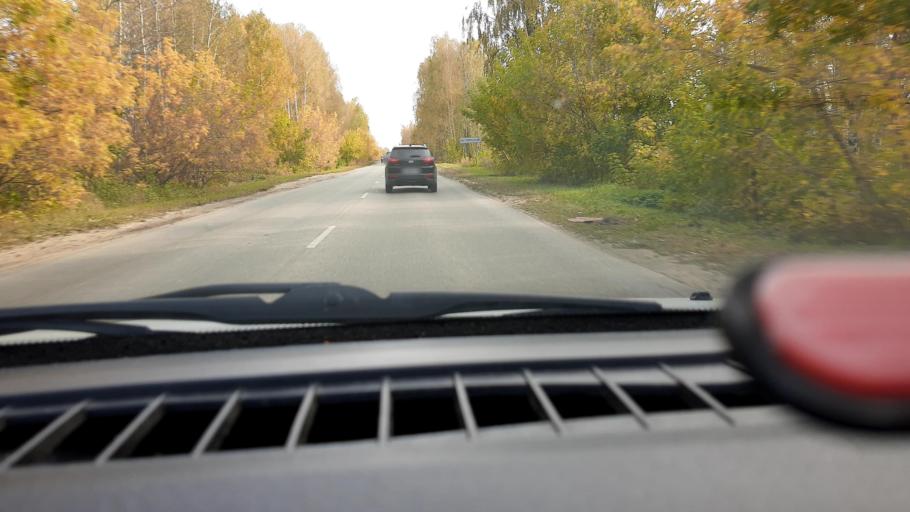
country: RU
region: Nizjnij Novgorod
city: Afonino
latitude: 56.3077
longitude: 44.1760
